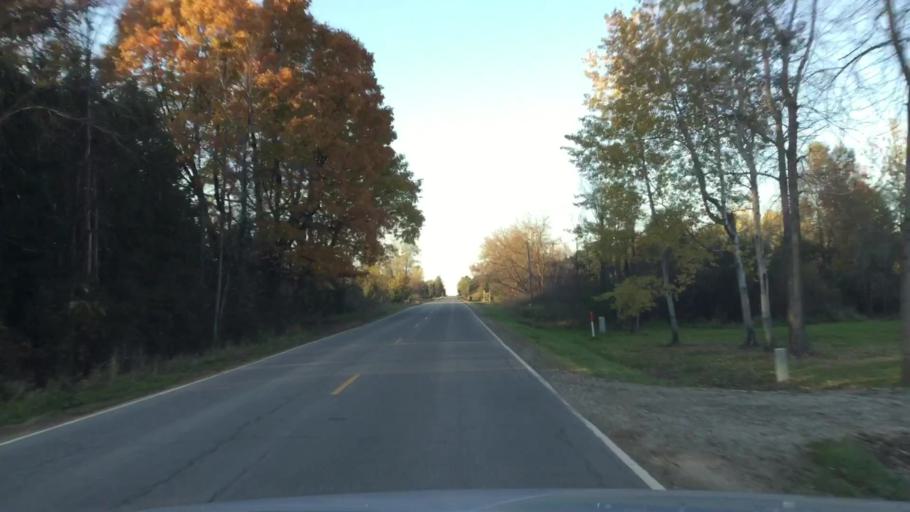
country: US
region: Michigan
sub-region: Sanilac County
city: Marlette
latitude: 43.3343
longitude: -83.1836
